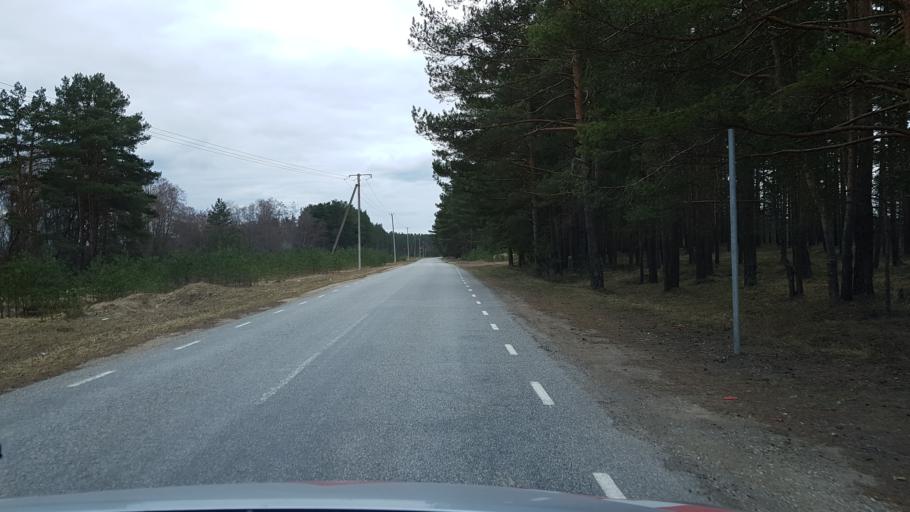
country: EE
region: Ida-Virumaa
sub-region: Narva linn
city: Narva
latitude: 59.4274
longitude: 28.1213
